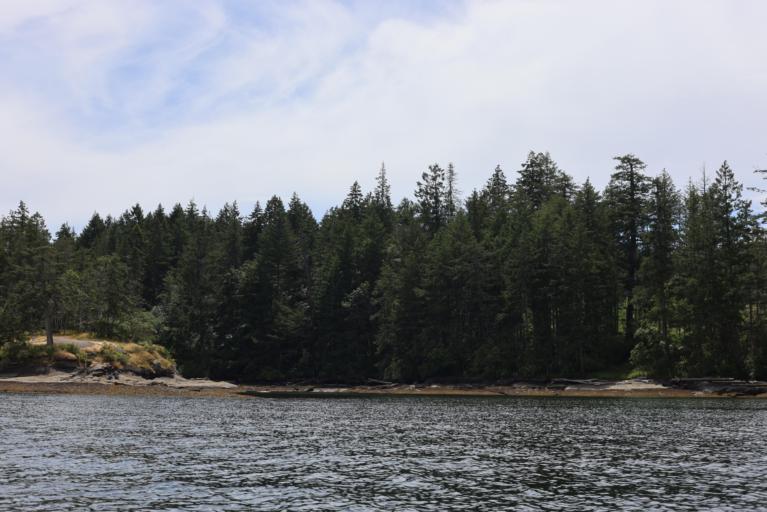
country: CA
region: British Columbia
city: Nanaimo
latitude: 49.1370
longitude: -123.8331
